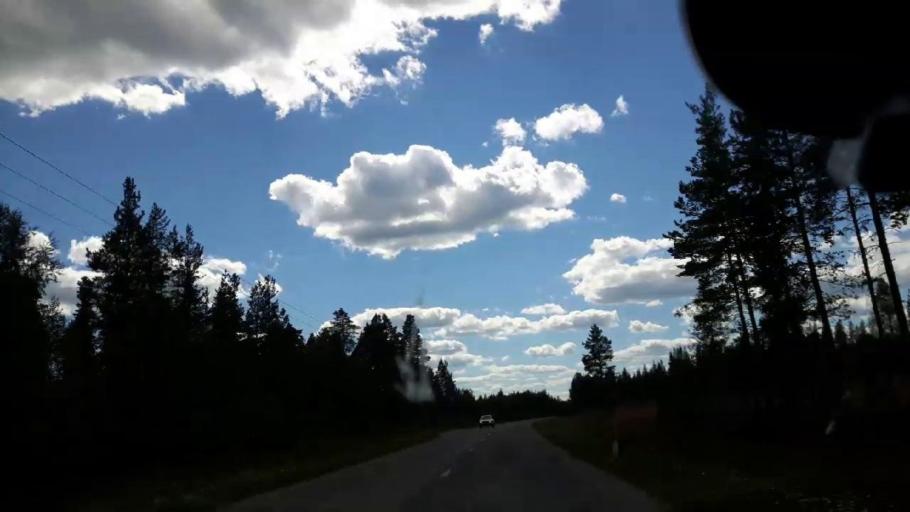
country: SE
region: Jaemtland
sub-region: Ragunda Kommun
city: Hammarstrand
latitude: 63.0032
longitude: 16.1142
